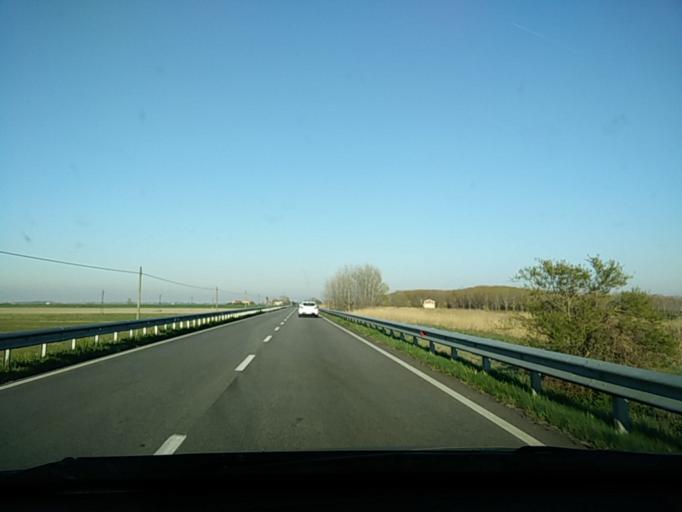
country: IT
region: Veneto
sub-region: Provincia di Venezia
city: Meolo
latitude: 45.5599
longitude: 12.4593
